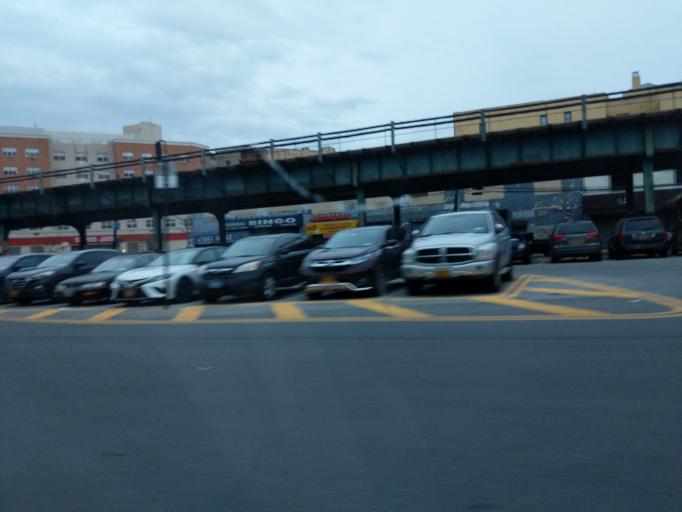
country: US
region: New York
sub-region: Bronx
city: The Bronx
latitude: 40.8509
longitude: -73.8682
